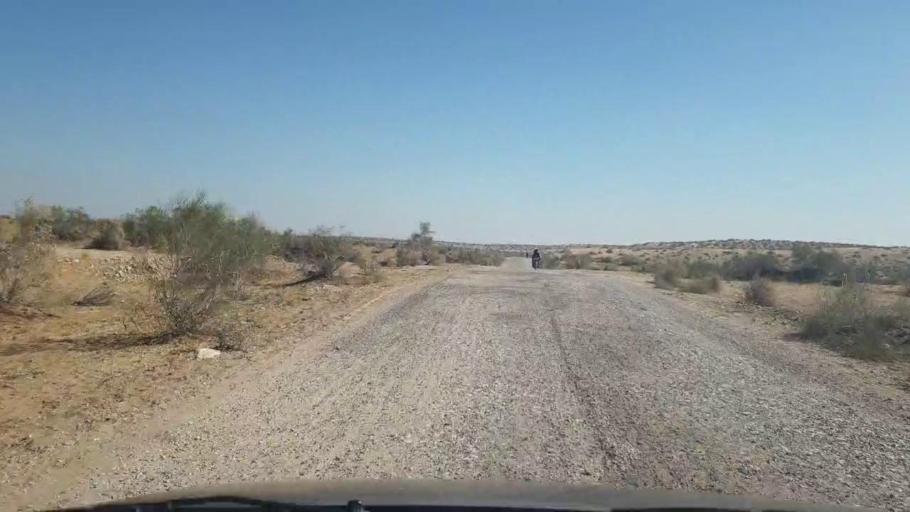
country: PK
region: Sindh
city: Bozdar
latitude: 27.0029
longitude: 68.8417
